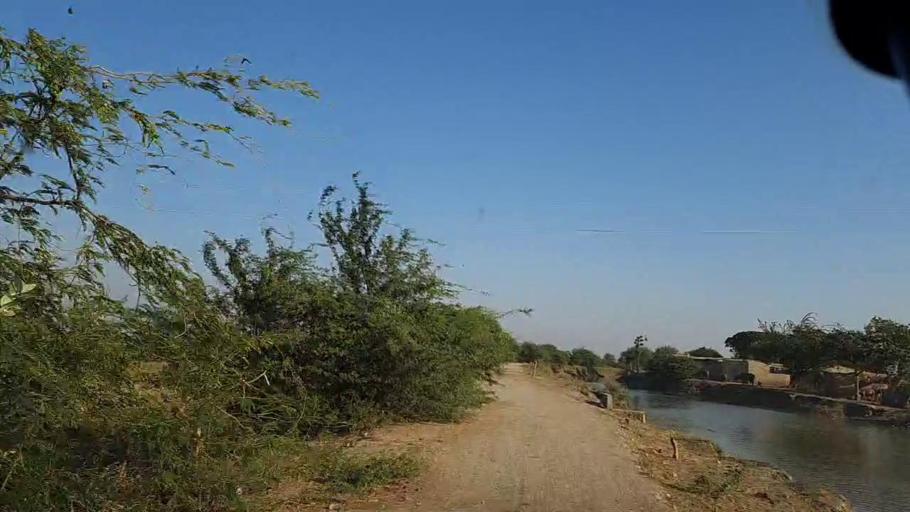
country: PK
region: Sindh
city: Chuhar Jamali
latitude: 24.5633
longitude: 68.0671
